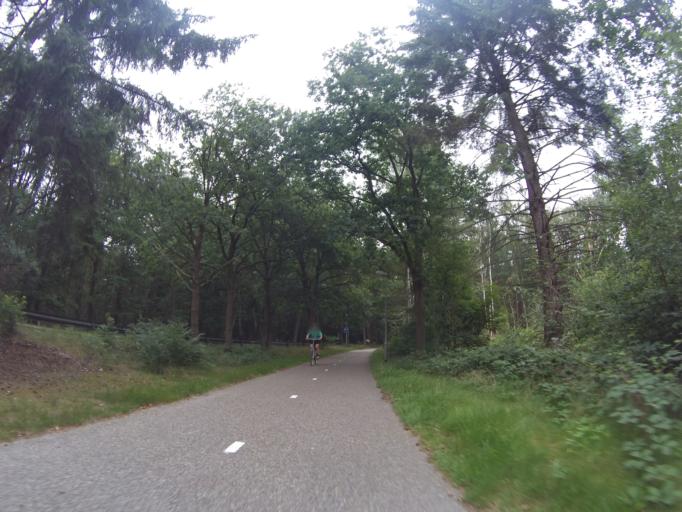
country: NL
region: North Holland
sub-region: Gemeente Laren
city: Laren
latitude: 52.2204
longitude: 5.2167
